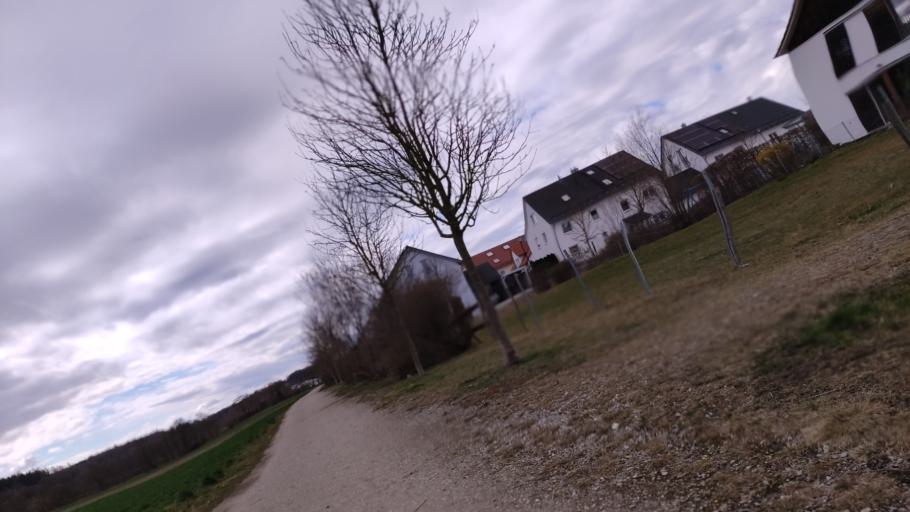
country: DE
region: Bavaria
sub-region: Upper Bavaria
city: Emmering
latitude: 48.1776
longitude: 11.2827
